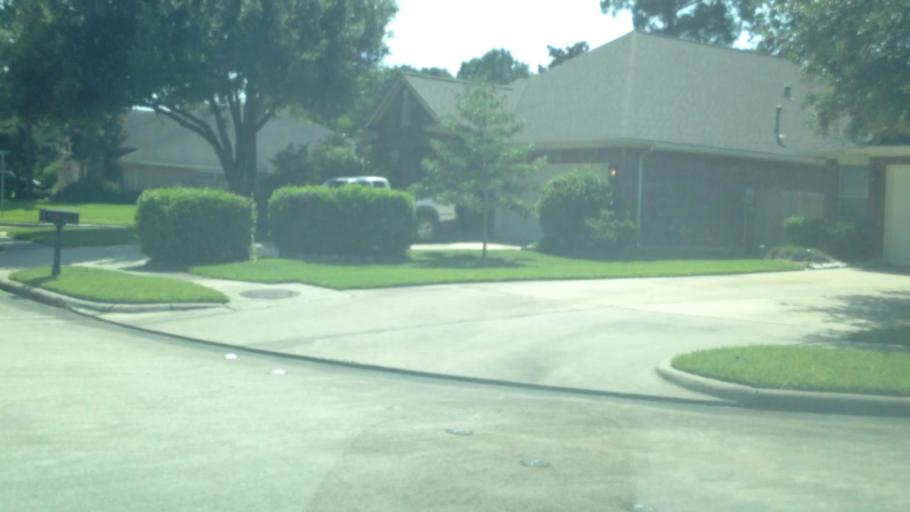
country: US
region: Texas
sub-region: Harris County
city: Atascocita
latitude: 29.9306
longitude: -95.1747
